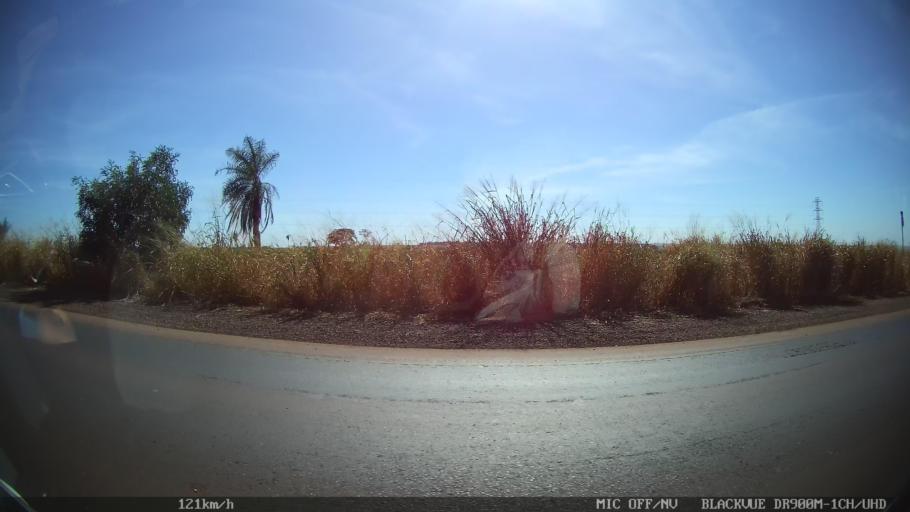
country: BR
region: Sao Paulo
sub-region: Barretos
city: Barretos
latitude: -20.4903
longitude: -48.5216
